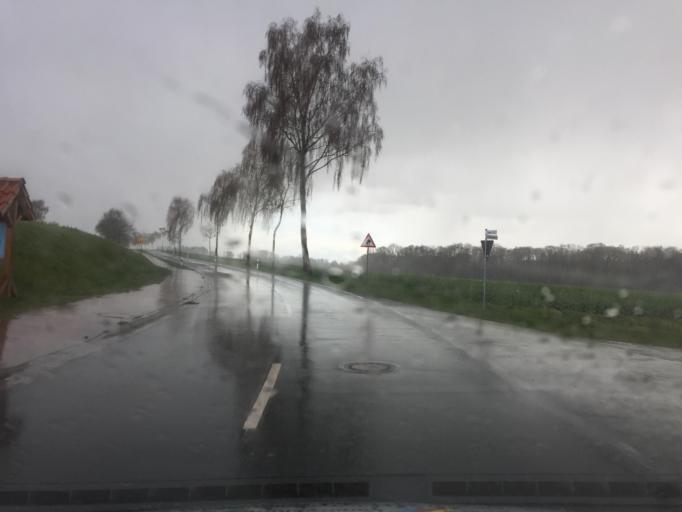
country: DE
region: Lower Saxony
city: Syke
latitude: 52.9306
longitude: 8.8826
